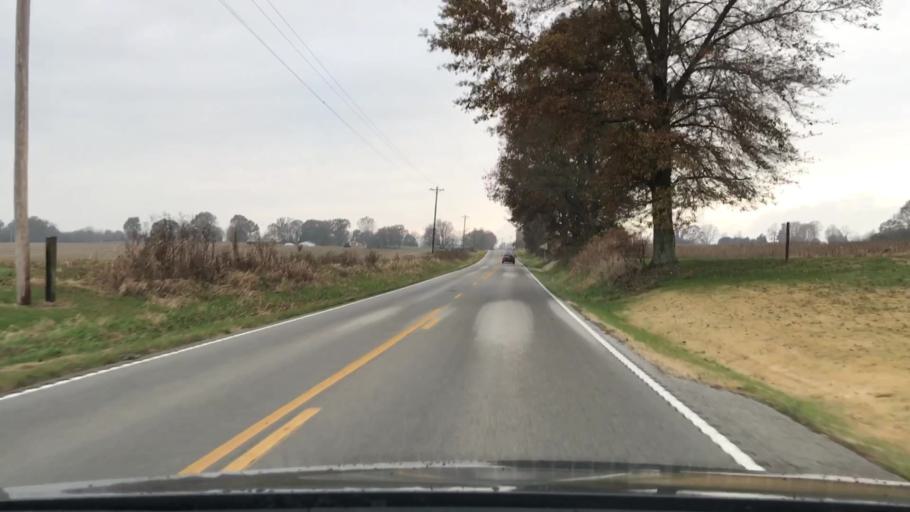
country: US
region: Kentucky
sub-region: Simpson County
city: Franklin
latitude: 36.7069
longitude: -86.4342
